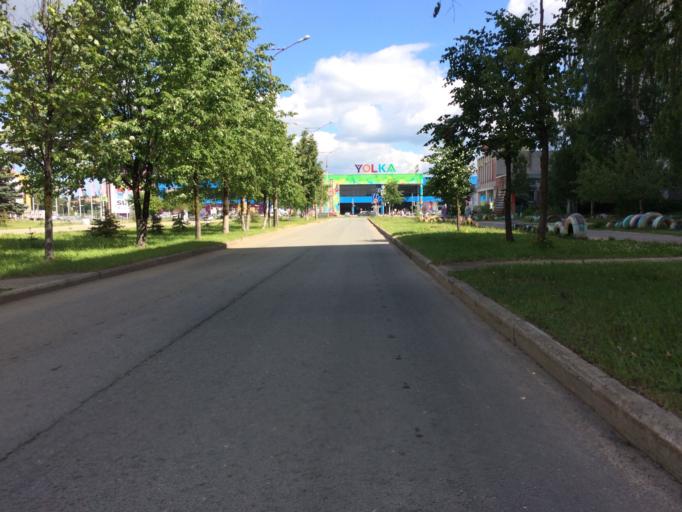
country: RU
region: Mariy-El
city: Yoshkar-Ola
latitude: 56.6289
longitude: 47.9254
